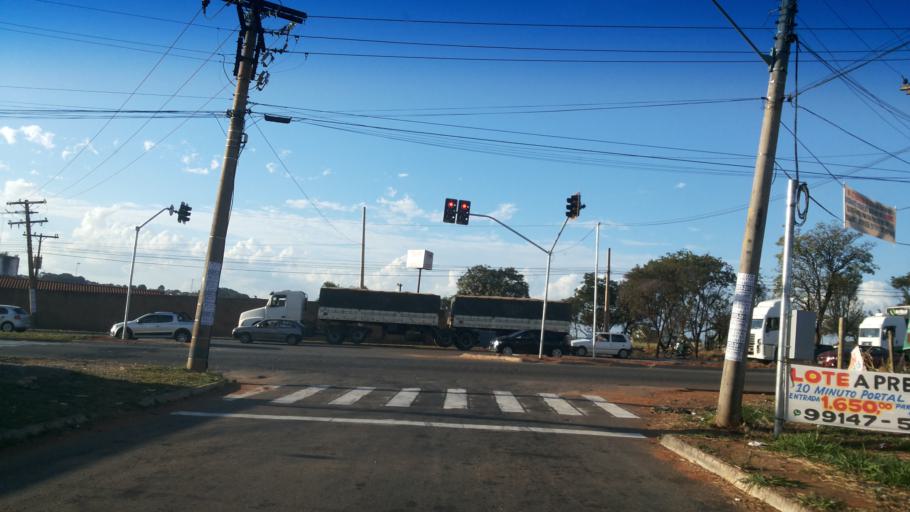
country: BR
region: Goias
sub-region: Goiania
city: Goiania
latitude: -16.6429
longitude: -49.3006
